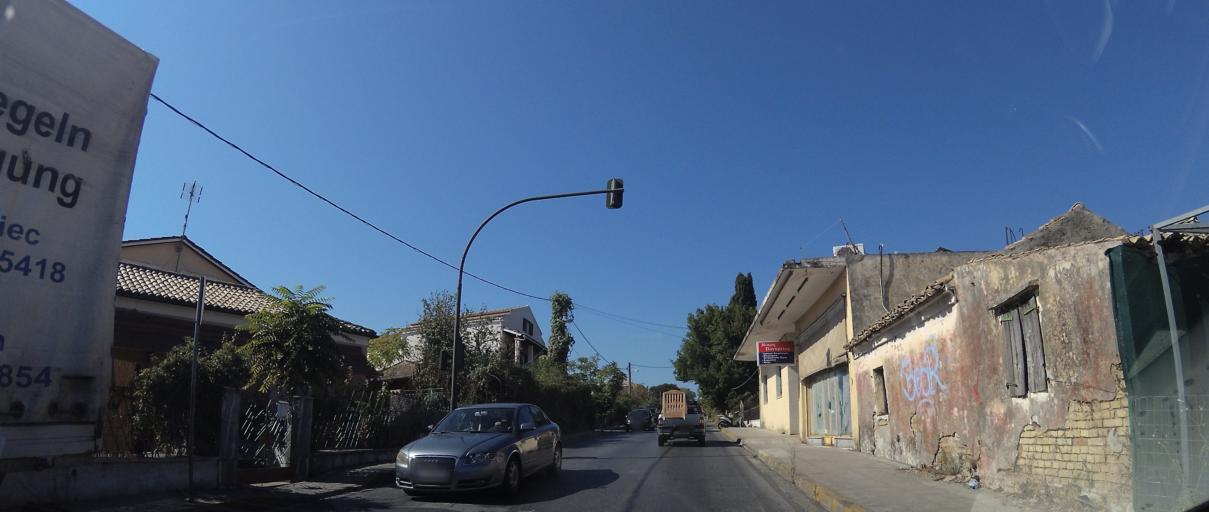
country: GR
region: Ionian Islands
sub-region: Nomos Kerkyras
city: Kerkyra
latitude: 39.6188
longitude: 19.9082
